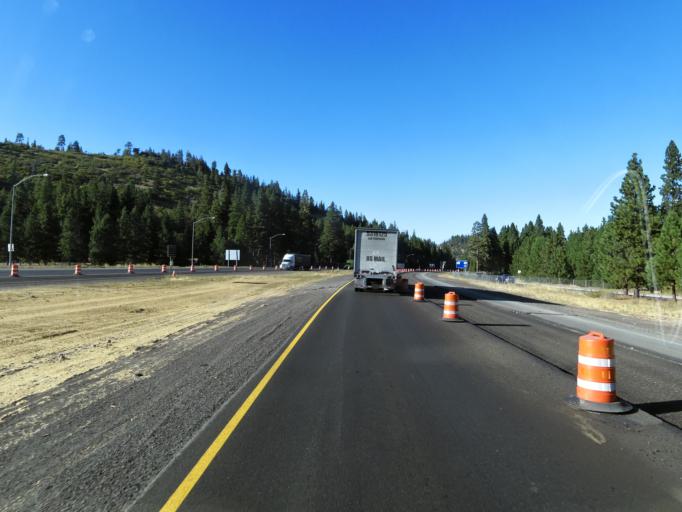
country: US
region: California
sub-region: Siskiyou County
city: Weed
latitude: 41.4015
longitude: -122.3836
